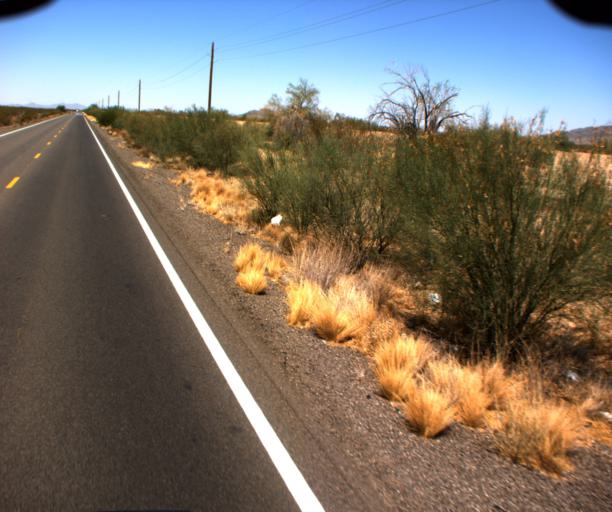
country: US
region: Arizona
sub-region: Pinal County
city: Maricopa
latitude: 33.0761
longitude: -112.1637
